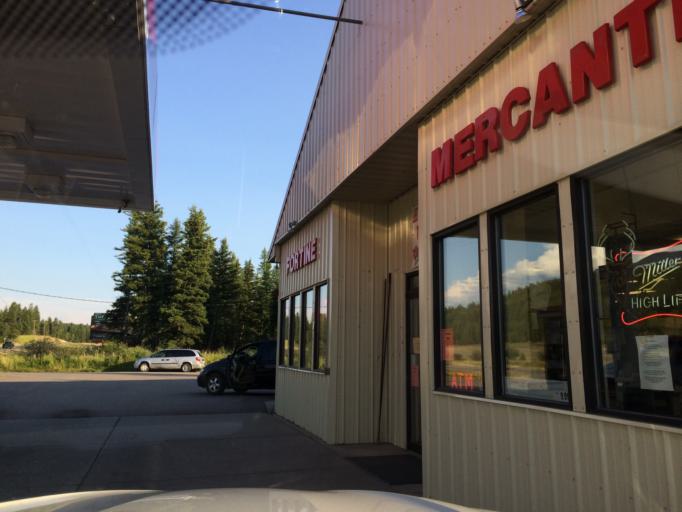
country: US
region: Montana
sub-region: Lincoln County
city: Eureka
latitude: 48.7560
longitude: -114.8873
